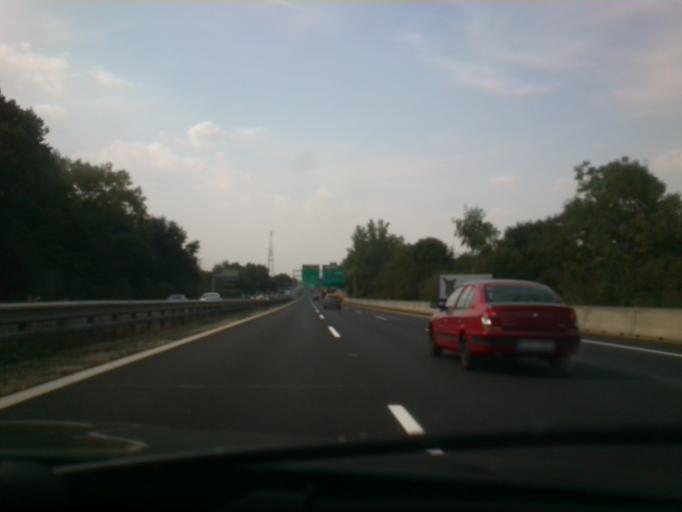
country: CZ
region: Central Bohemia
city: Velke Popovice
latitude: 49.9588
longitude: 14.6331
